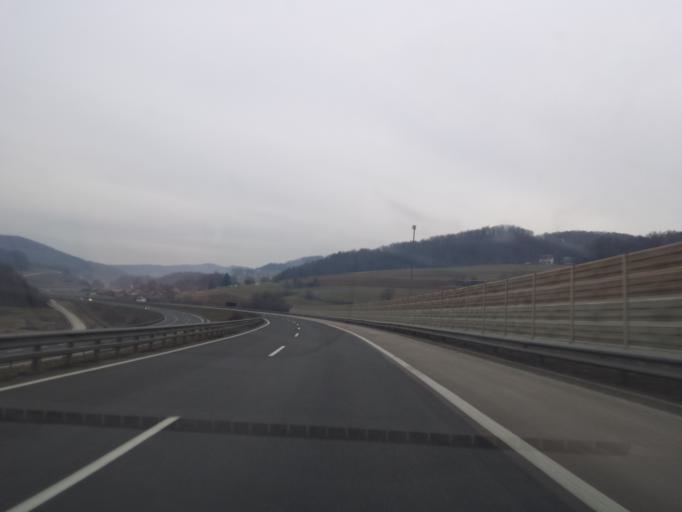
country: SI
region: Mirna Pec
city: Mirna Pec
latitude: 45.8622
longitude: 15.1393
